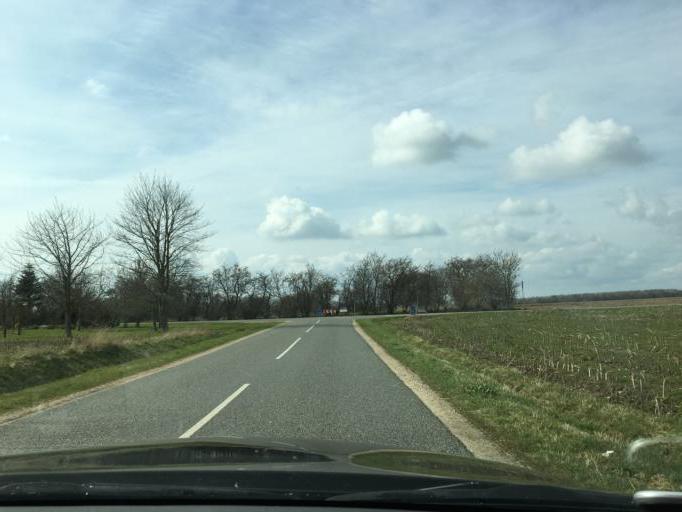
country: DK
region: South Denmark
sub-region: Esbjerg Kommune
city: Bramming
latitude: 55.5002
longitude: 8.6724
